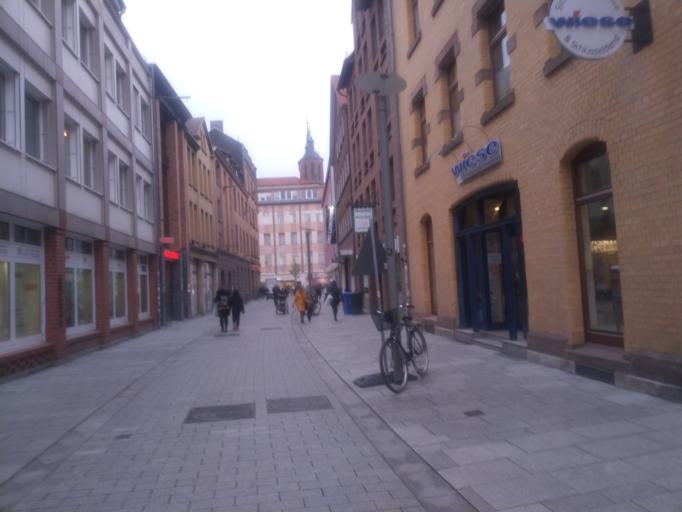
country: DE
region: Lower Saxony
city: Goettingen
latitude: 51.5312
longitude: 9.9333
